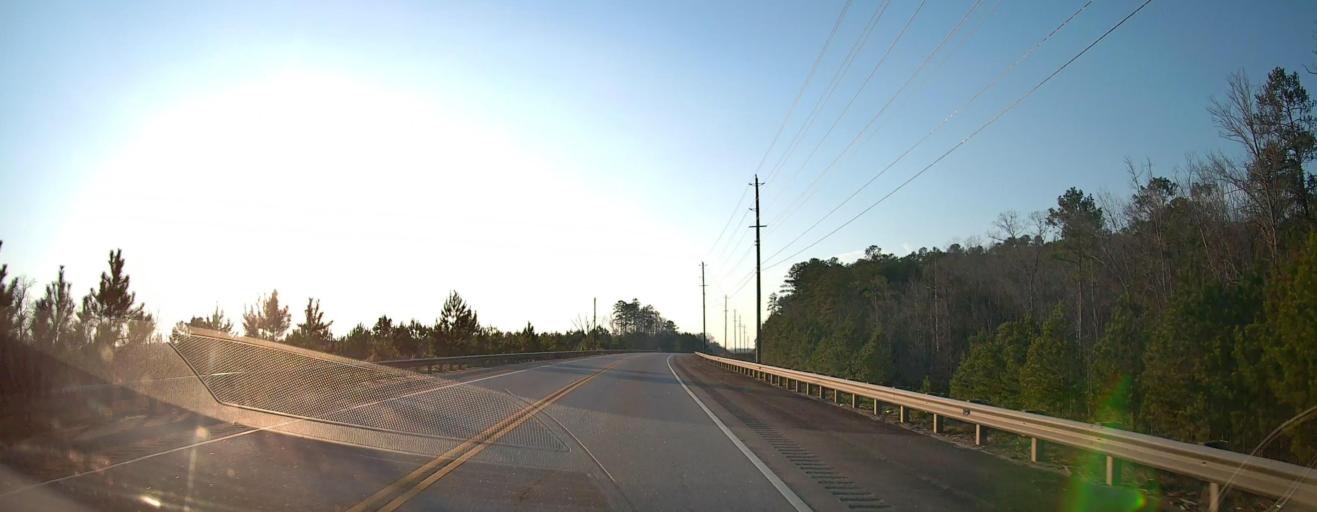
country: US
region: Georgia
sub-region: Troup County
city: La Grange
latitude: 32.9903
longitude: -85.0677
